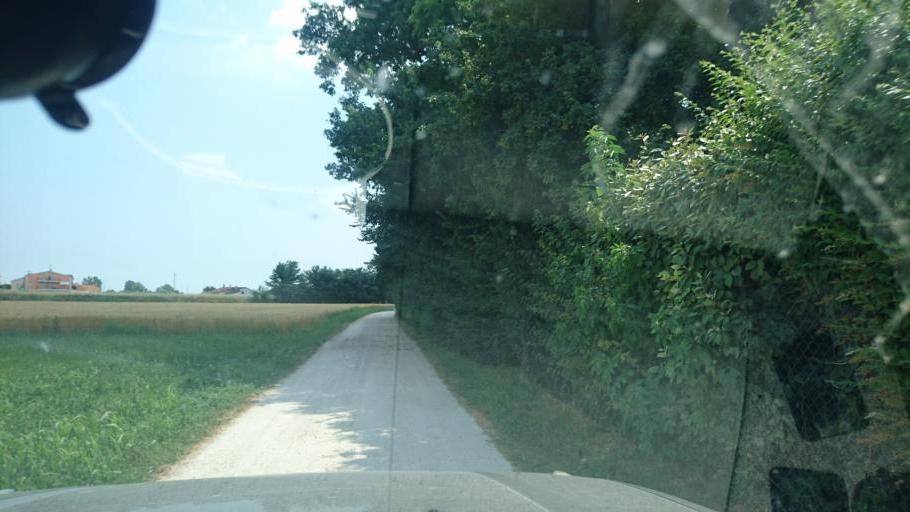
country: IT
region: Veneto
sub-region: Provincia di Padova
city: Monselice
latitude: 45.2235
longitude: 11.7353
